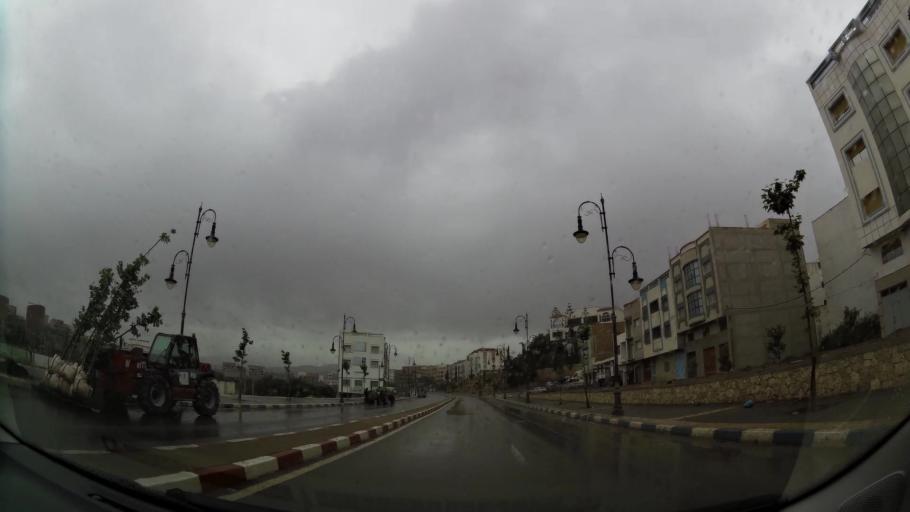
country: MA
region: Taza-Al Hoceima-Taounate
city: Imzourene
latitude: 35.1483
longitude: -3.8478
